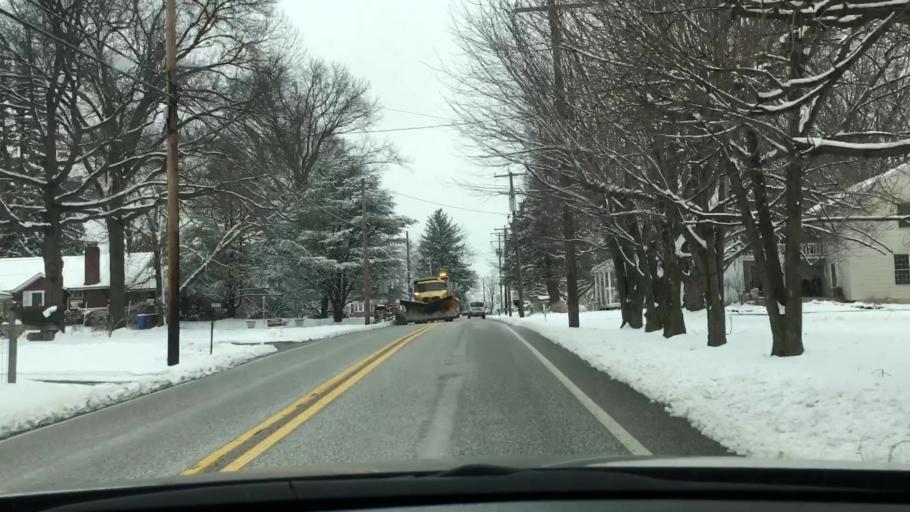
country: US
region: Pennsylvania
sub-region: York County
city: East York
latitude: 39.9960
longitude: -76.7065
